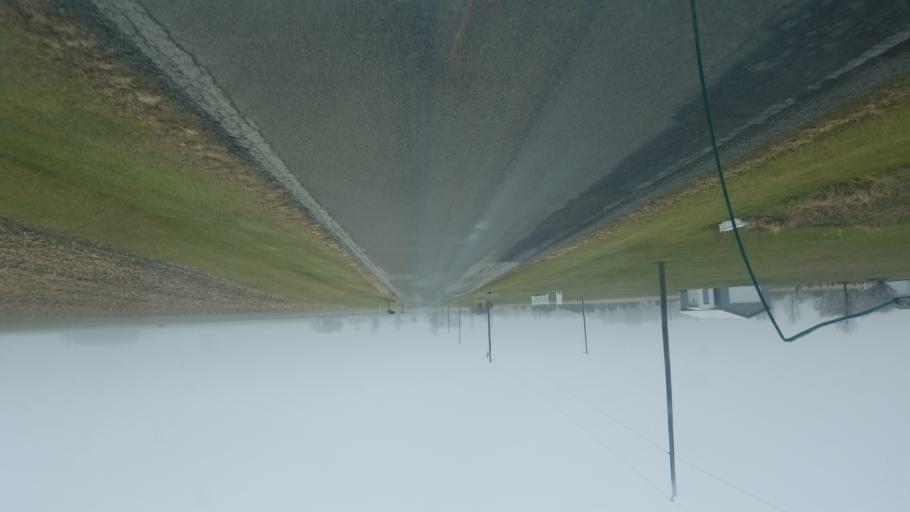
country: US
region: Ohio
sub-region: Champaign County
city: North Lewisburg
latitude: 40.3789
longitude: -83.5246
